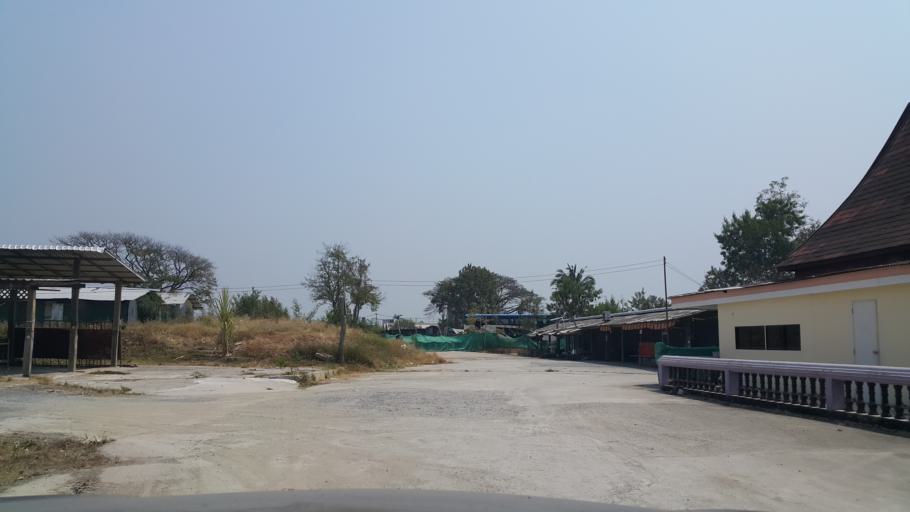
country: TH
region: Chiang Mai
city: Saraphi
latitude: 18.7636
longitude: 99.0355
